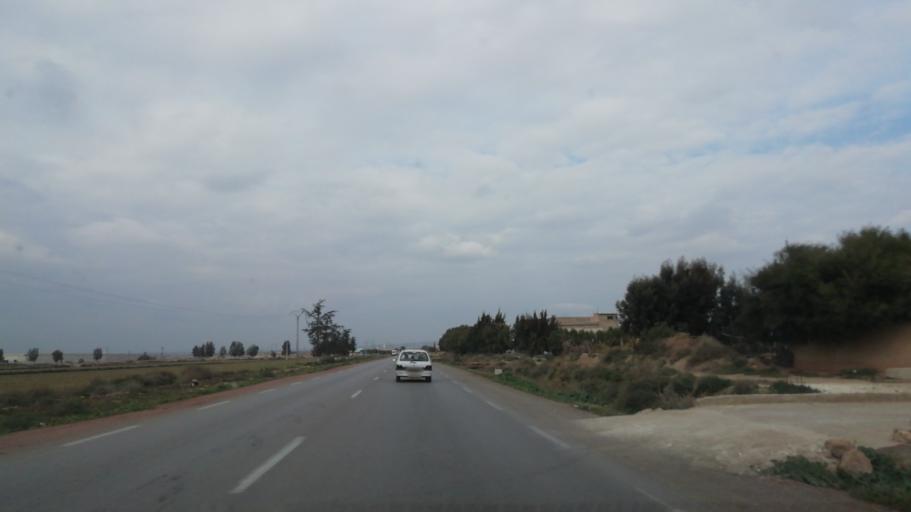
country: DZ
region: Mostaganem
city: Mostaganem
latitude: 35.6892
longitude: 0.0562
